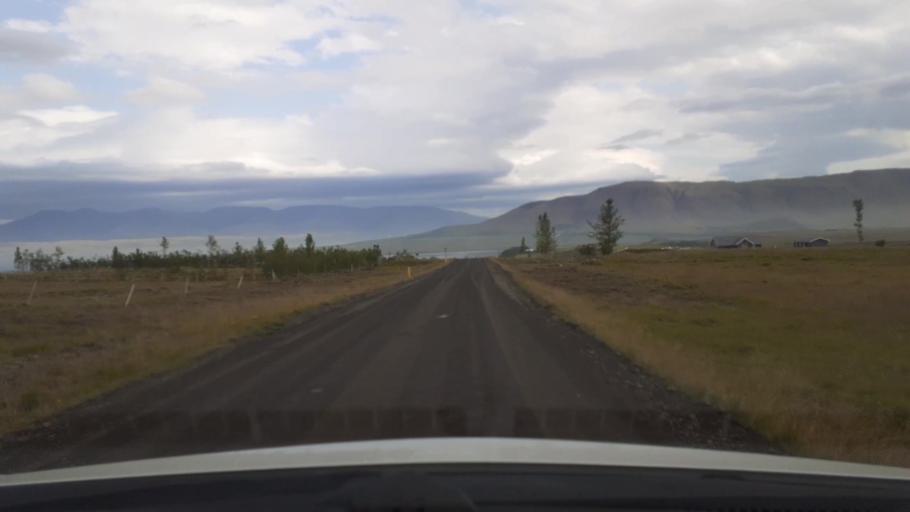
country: IS
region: Capital Region
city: Mosfellsbaer
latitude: 64.3163
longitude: -21.6514
